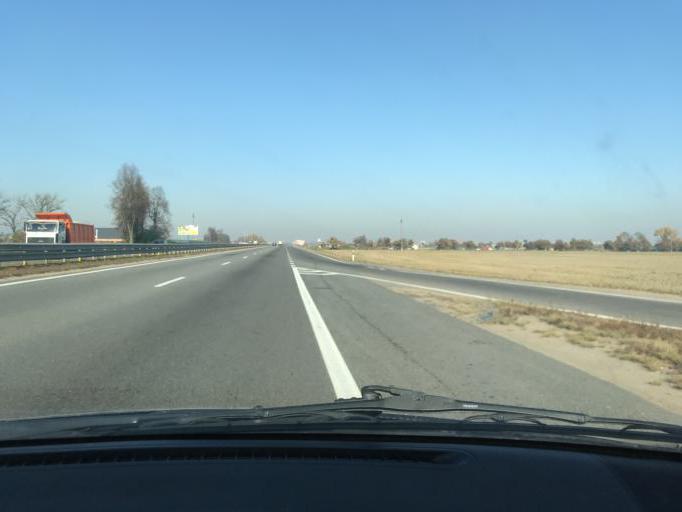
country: BY
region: Minsk
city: Yubilyeyny
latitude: 53.7899
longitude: 27.5279
